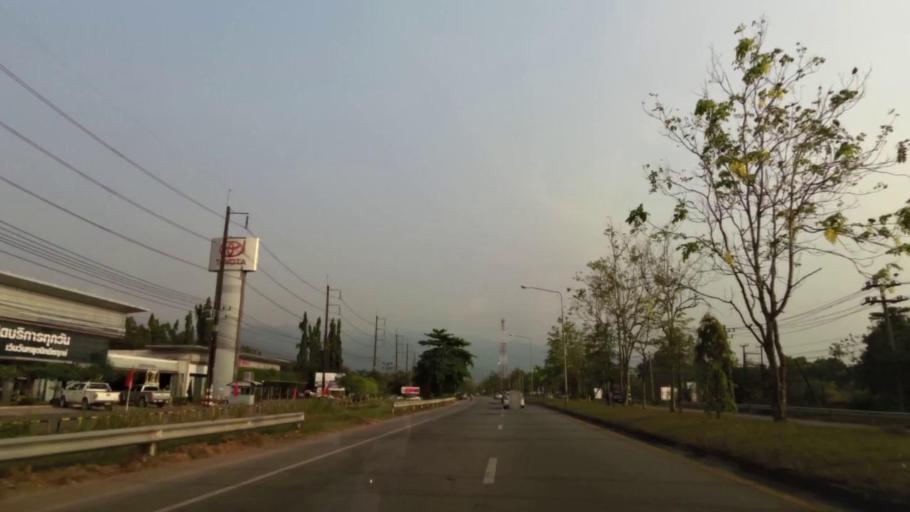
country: TH
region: Chanthaburi
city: Chanthaburi
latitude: 12.5973
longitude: 102.1414
